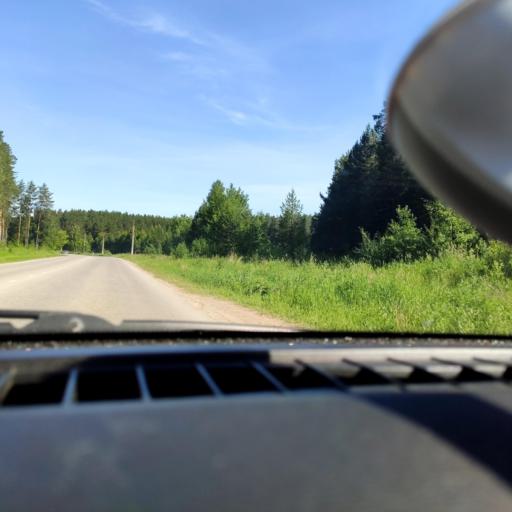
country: RU
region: Perm
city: Overyata
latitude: 58.0063
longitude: 55.8766
